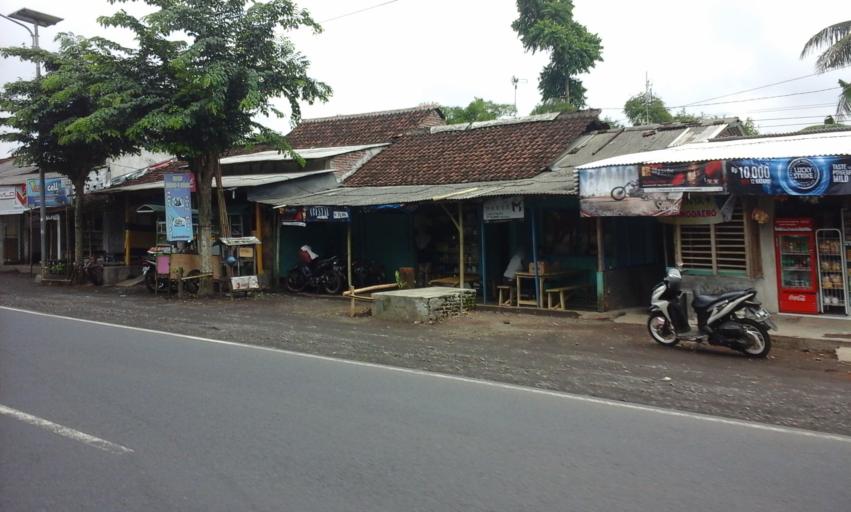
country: ID
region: East Java
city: Pringgowirawan
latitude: -8.1331
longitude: 113.4125
